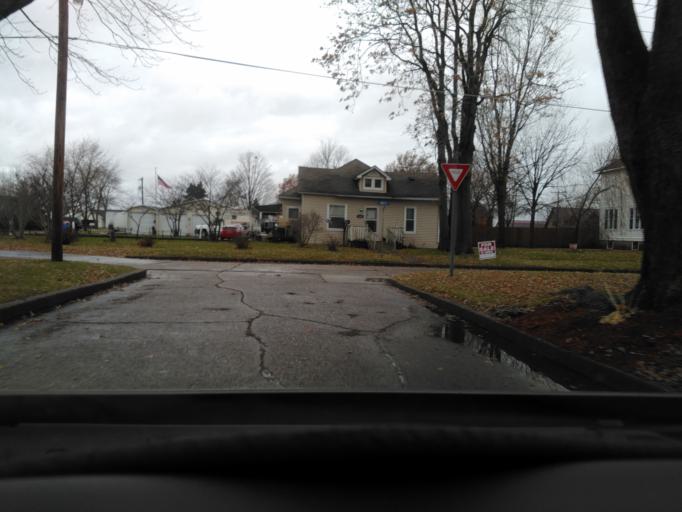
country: US
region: Illinois
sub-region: Effingham County
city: Altamont
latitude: 39.0612
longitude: -88.7552
